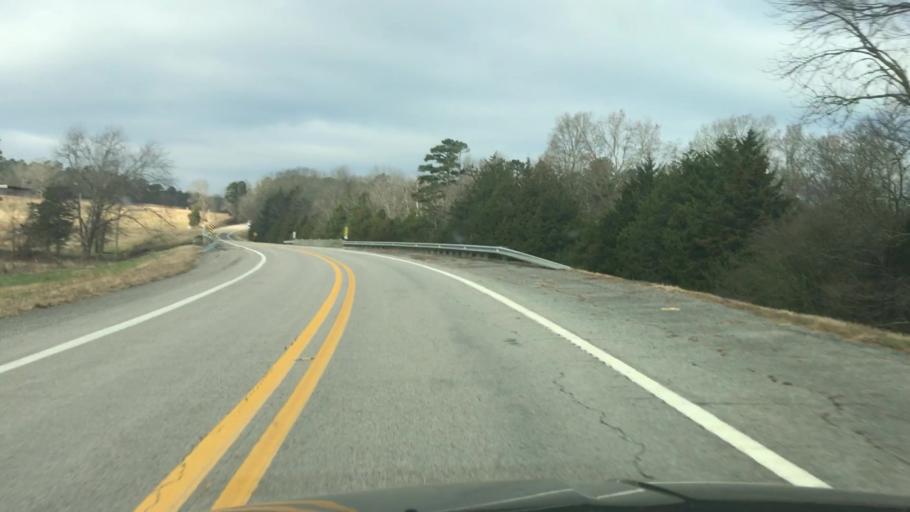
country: US
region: Arkansas
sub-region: Montgomery County
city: Mount Ida
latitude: 34.6590
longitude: -93.7627
